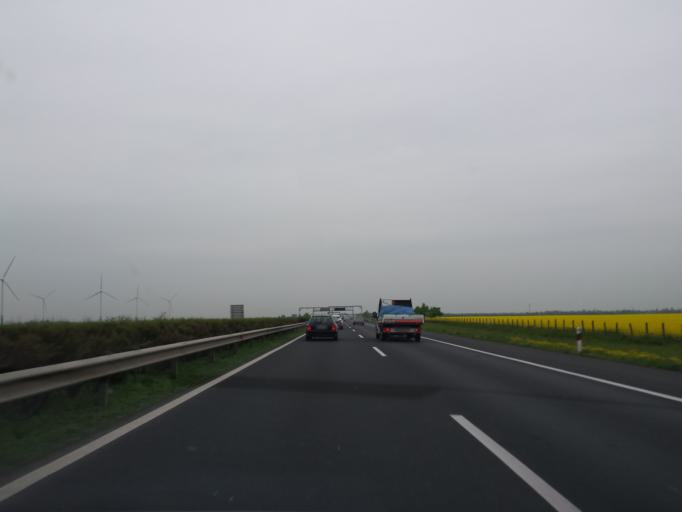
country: HU
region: Gyor-Moson-Sopron
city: Mosonmagyarovar
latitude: 47.8768
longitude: 17.2058
